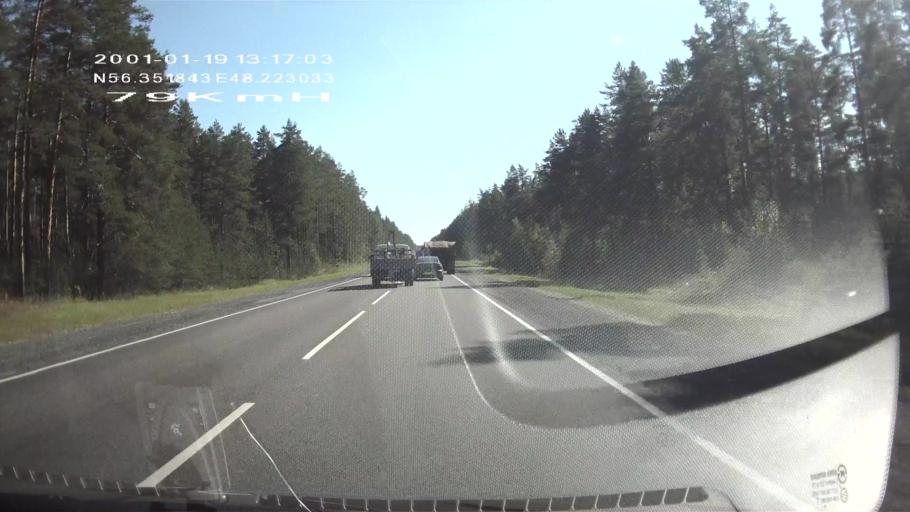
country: RU
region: Mariy-El
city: Suslonger
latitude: 56.3518
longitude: 48.2231
